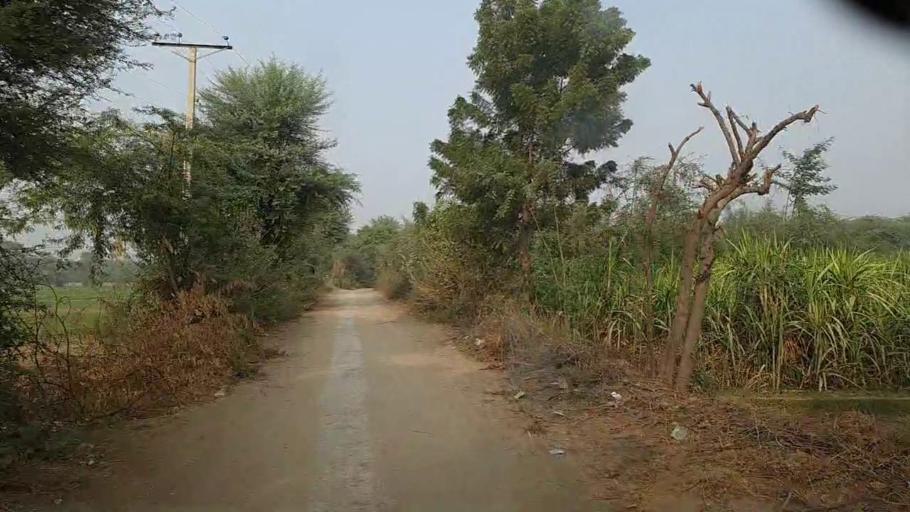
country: PK
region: Sindh
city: Bozdar
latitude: 27.1485
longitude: 68.6703
